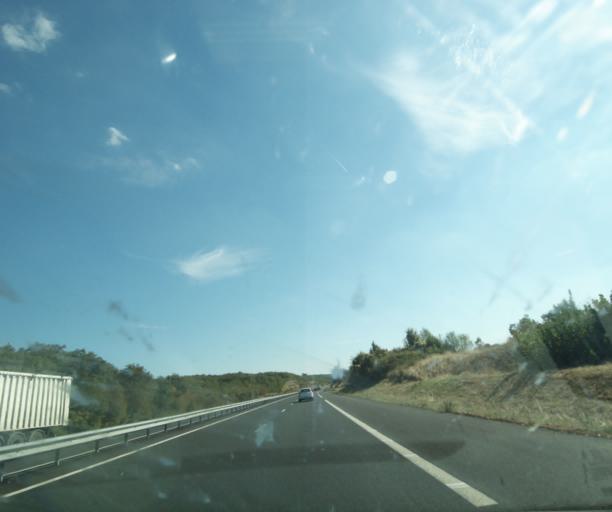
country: FR
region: Limousin
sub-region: Departement de la Correze
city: Brive-la-Gaillarde
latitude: 45.0447
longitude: 1.5188
